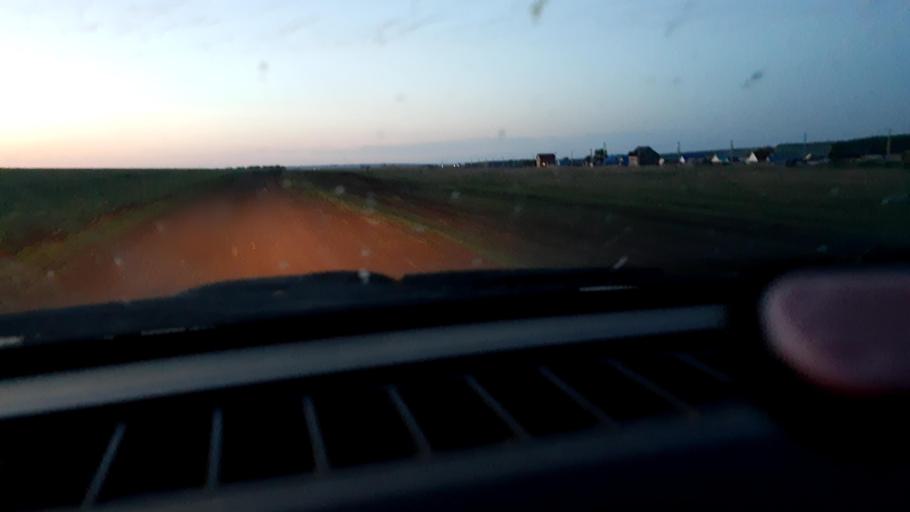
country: RU
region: Bashkortostan
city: Asanovo
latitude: 54.8561
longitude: 55.5854
